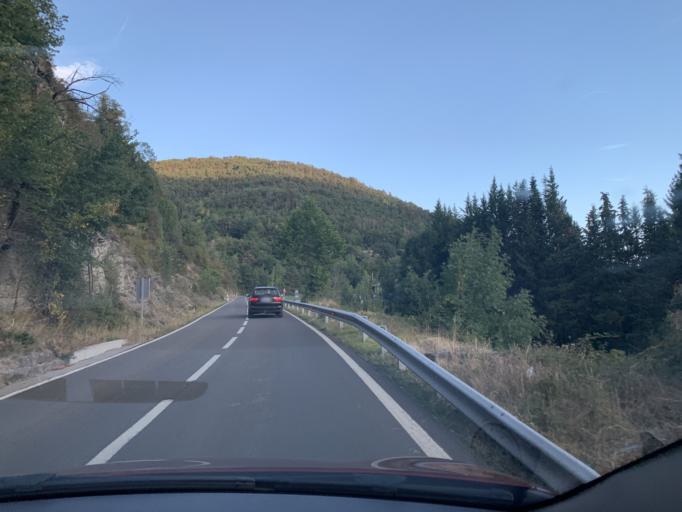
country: ES
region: Aragon
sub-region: Provincia de Huesca
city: Broto
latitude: 42.5994
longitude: -0.1187
